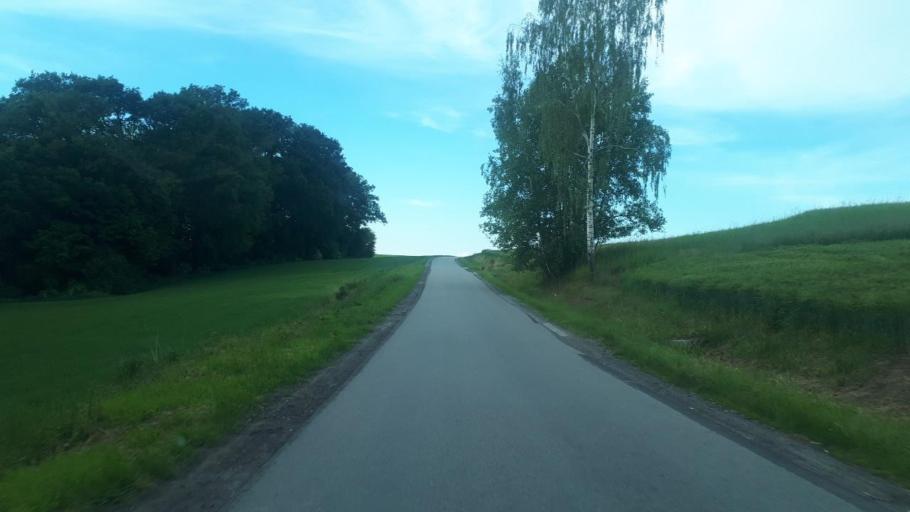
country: PL
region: Silesian Voivodeship
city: Janowice
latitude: 49.9005
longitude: 19.1104
